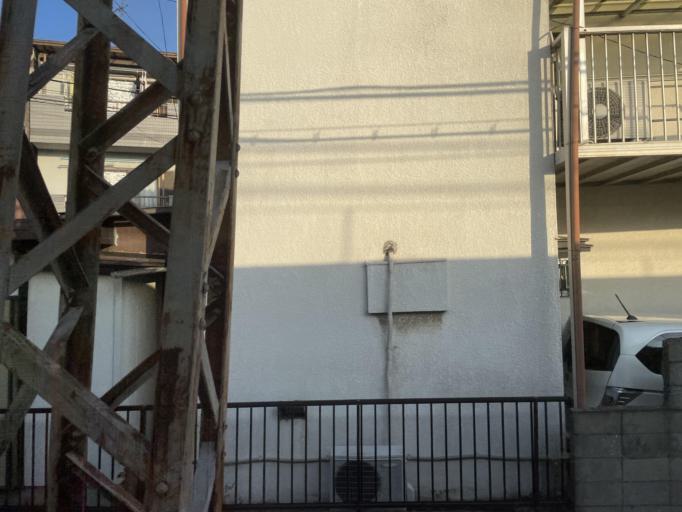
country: JP
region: Osaka
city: Daitocho
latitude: 34.6656
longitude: 135.6471
